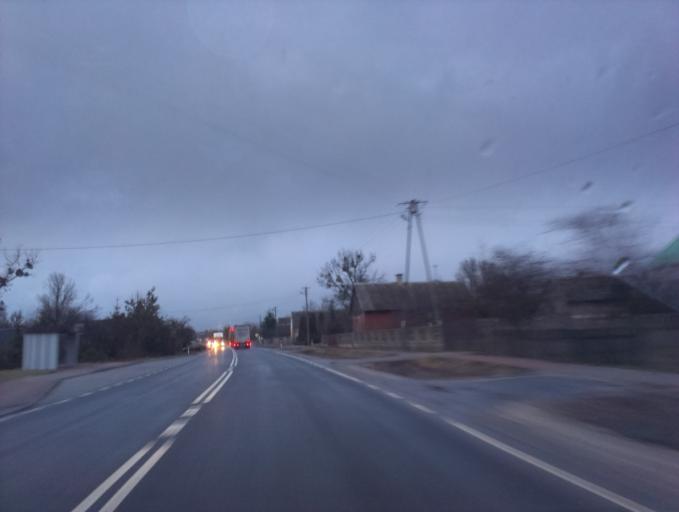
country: PL
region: Lodz Voivodeship
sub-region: Powiat opoczynski
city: Zarnow
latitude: 51.2127
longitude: 20.1953
